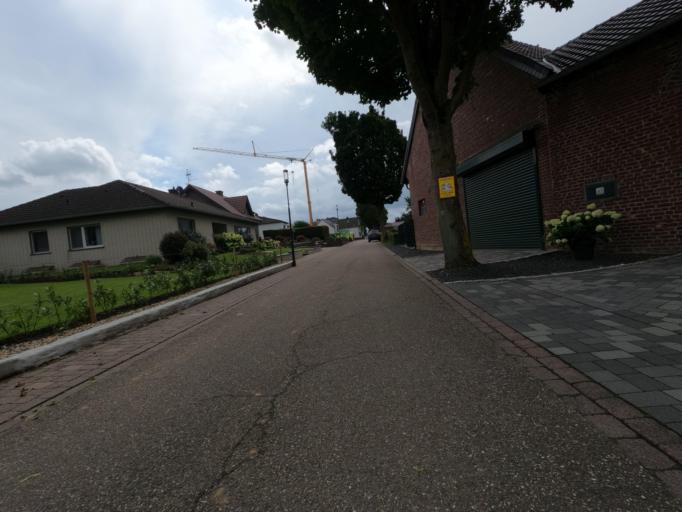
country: DE
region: North Rhine-Westphalia
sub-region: Regierungsbezirk Koln
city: Gangelt
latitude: 51.0055
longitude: 6.0240
